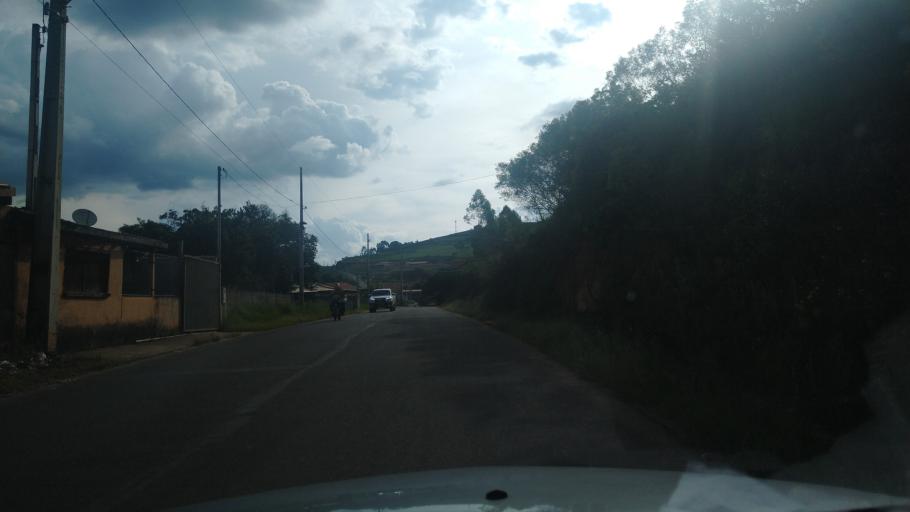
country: BR
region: Minas Gerais
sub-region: Extrema
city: Extrema
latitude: -22.7312
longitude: -46.3615
